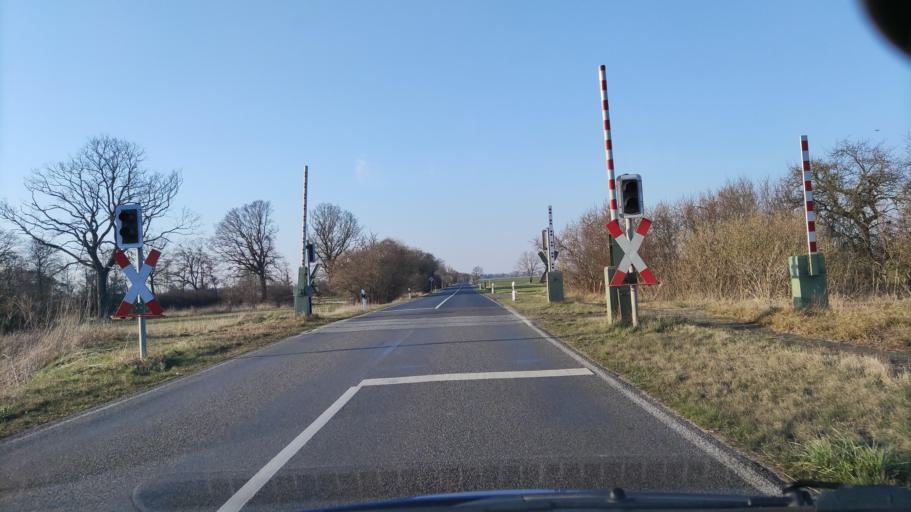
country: DE
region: Brandenburg
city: Cumlosen
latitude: 52.9381
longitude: 11.6658
